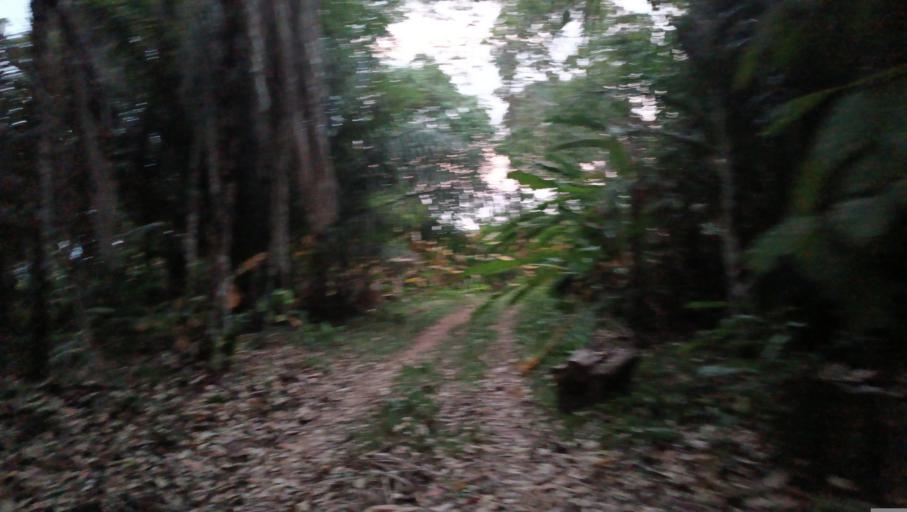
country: BO
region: La Paz
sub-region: Provincia Larecaja
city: Guanay
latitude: -15.5682
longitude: -67.3275
